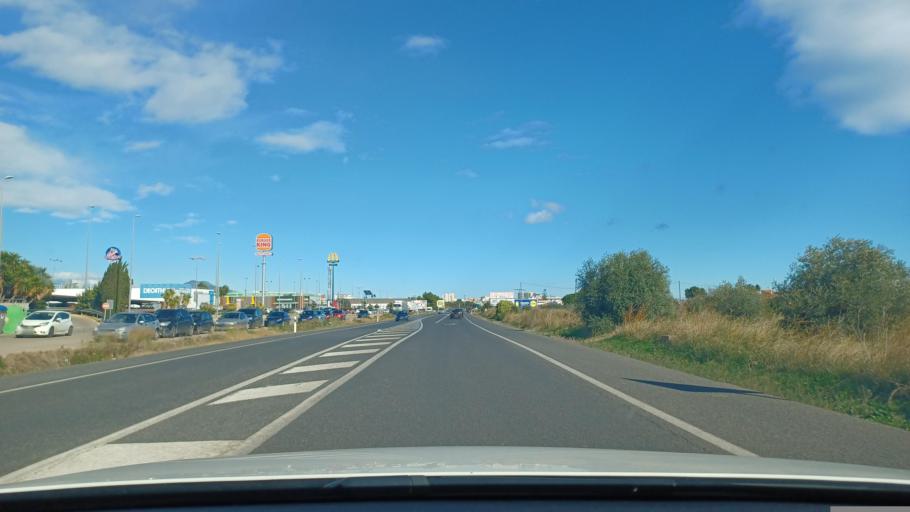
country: ES
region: Valencia
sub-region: Provincia de Castello
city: Vinaros
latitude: 40.4533
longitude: 0.4523
